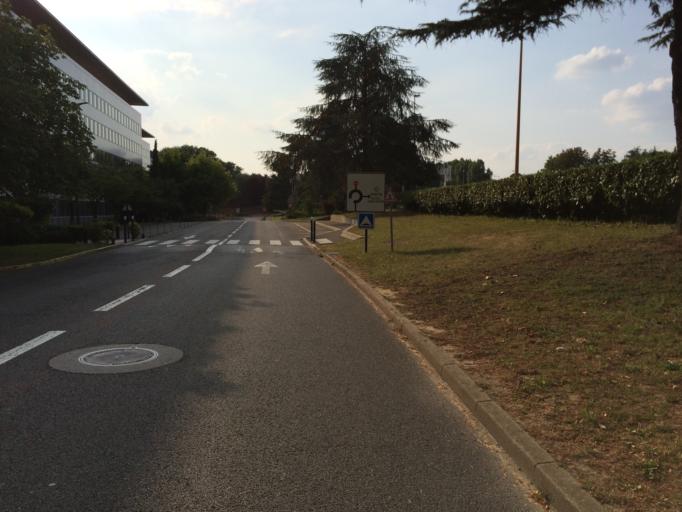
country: FR
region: Ile-de-France
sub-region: Departement de l'Essonne
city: Bievres
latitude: 48.7745
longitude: 2.2398
